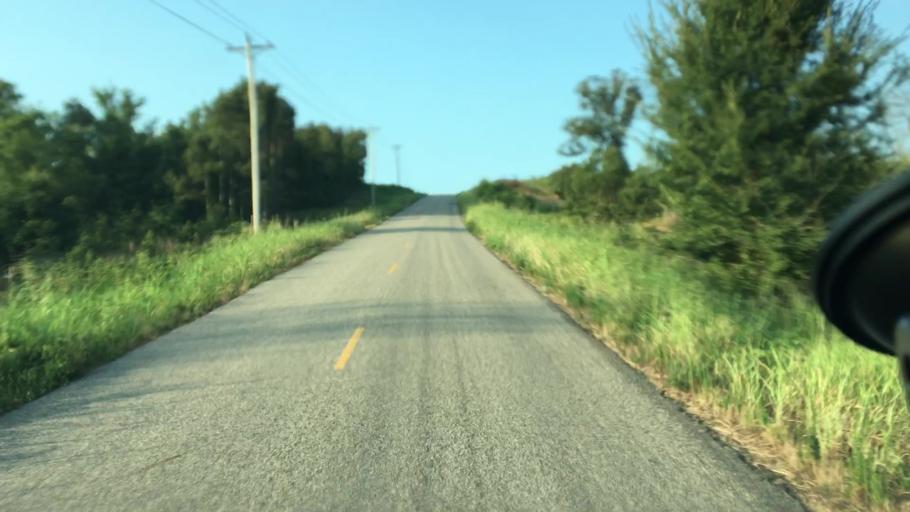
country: US
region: Arkansas
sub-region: Johnson County
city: Coal Hill
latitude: 35.3595
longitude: -93.6131
